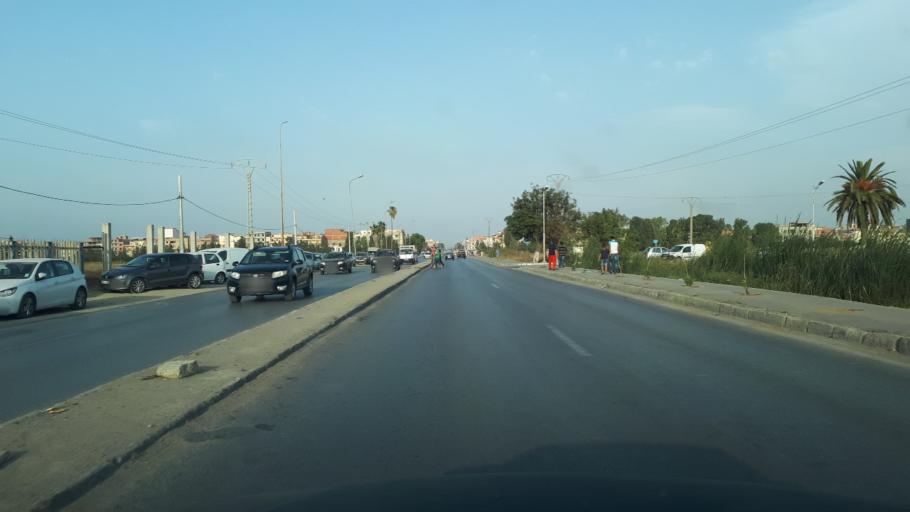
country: DZ
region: Alger
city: Dar el Beida
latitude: 36.7292
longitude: 3.2254
